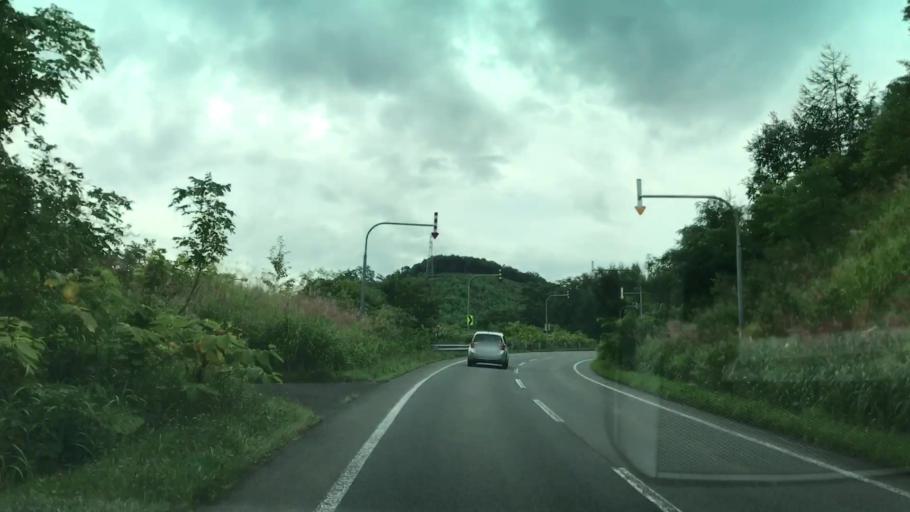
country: JP
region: Hokkaido
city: Yoichi
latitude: 43.1450
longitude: 140.8208
